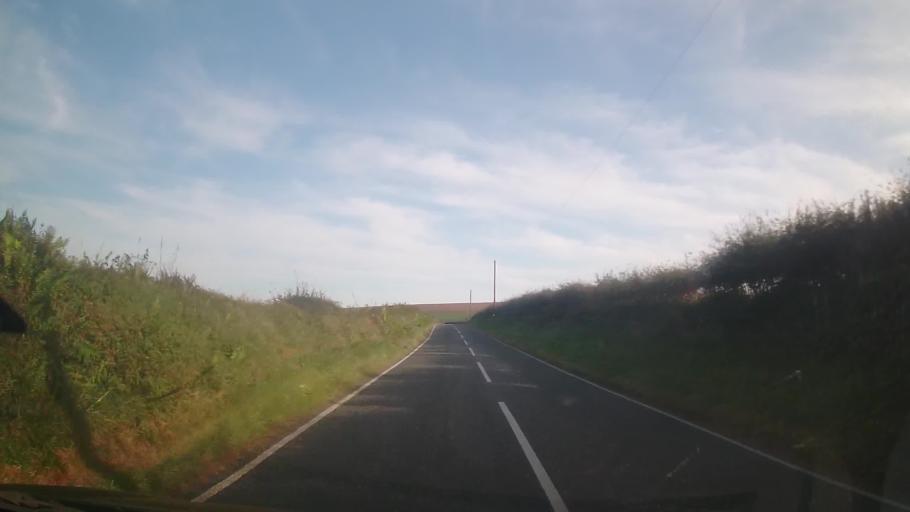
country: GB
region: Wales
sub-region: Pembrokeshire
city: Ambleston
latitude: 51.9682
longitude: -4.9034
